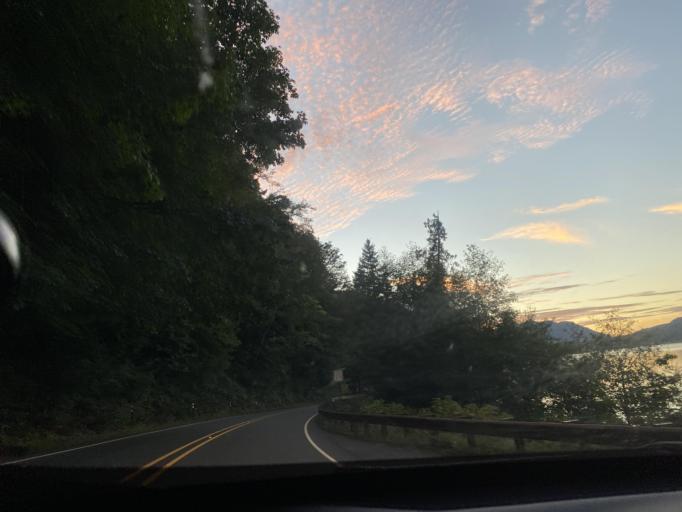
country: CA
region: British Columbia
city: Sooke
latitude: 48.0771
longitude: -123.7570
